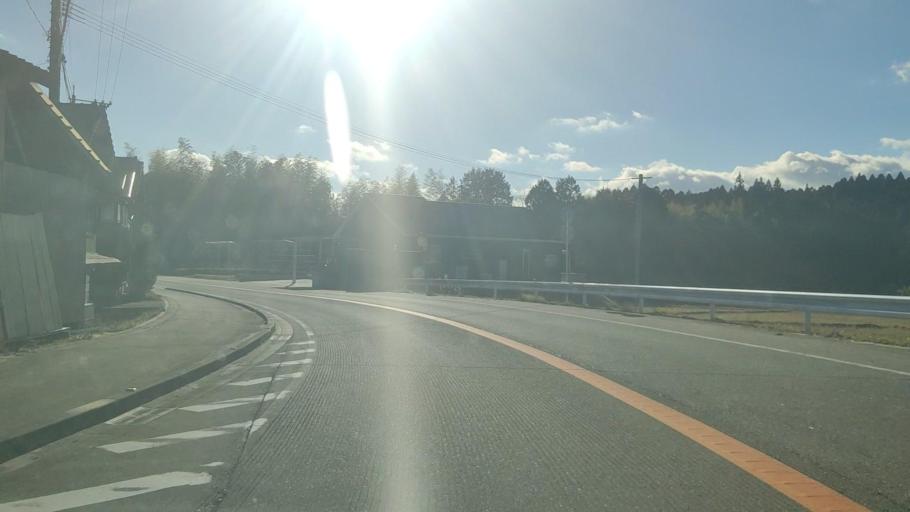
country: JP
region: Fukuoka
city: Maebaru-chuo
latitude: 33.4442
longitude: 130.2693
